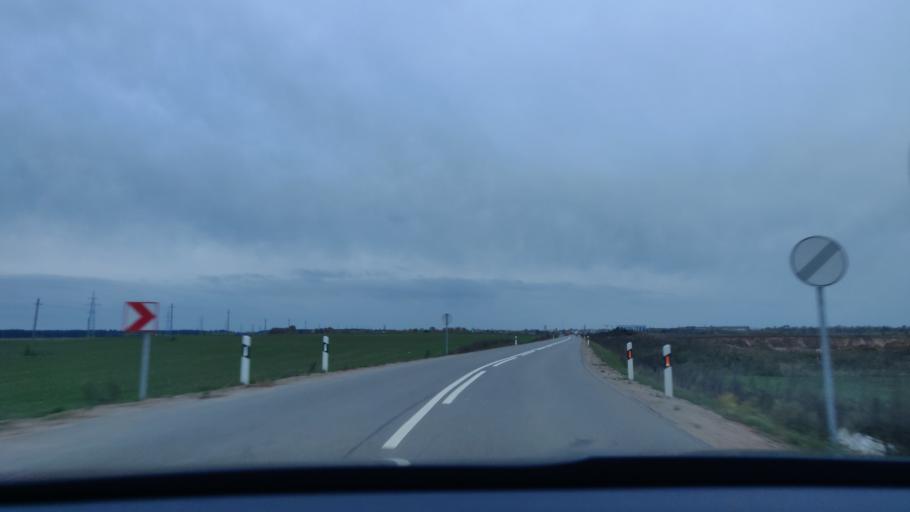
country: LT
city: Lentvaris
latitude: 54.6011
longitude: 25.0096
